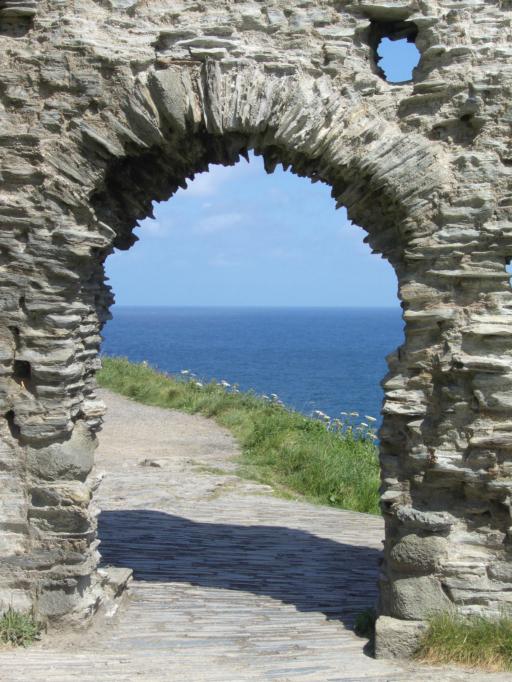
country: GB
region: England
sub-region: Cornwall
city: Tintagel
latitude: 50.6682
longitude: -4.7598
